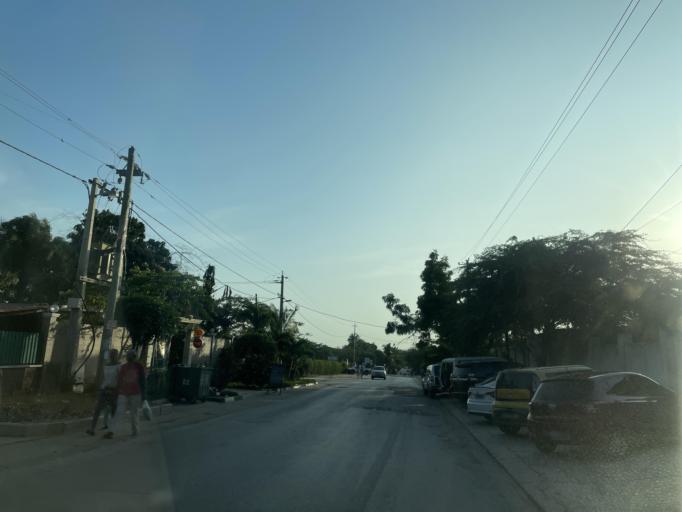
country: AO
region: Luanda
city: Luanda
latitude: -8.9085
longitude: 13.2294
